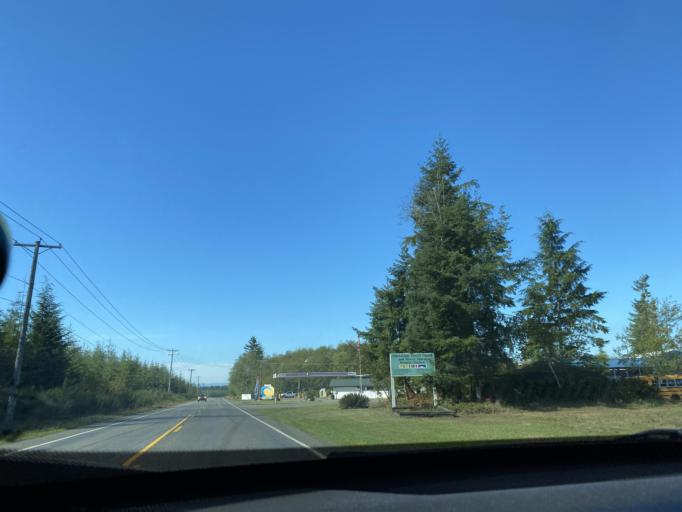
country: US
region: Washington
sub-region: Clallam County
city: Forks
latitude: 47.9665
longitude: -124.4099
